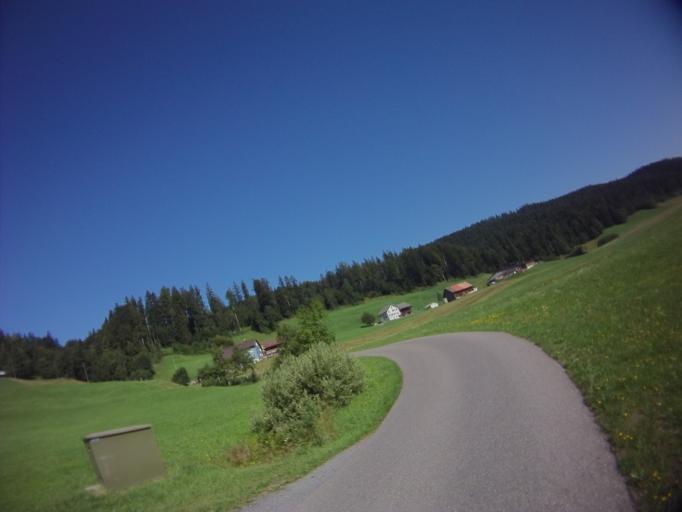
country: CH
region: Schwyz
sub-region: Bezirk Schwyz
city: Rothenthurm
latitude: 47.1225
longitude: 8.6691
